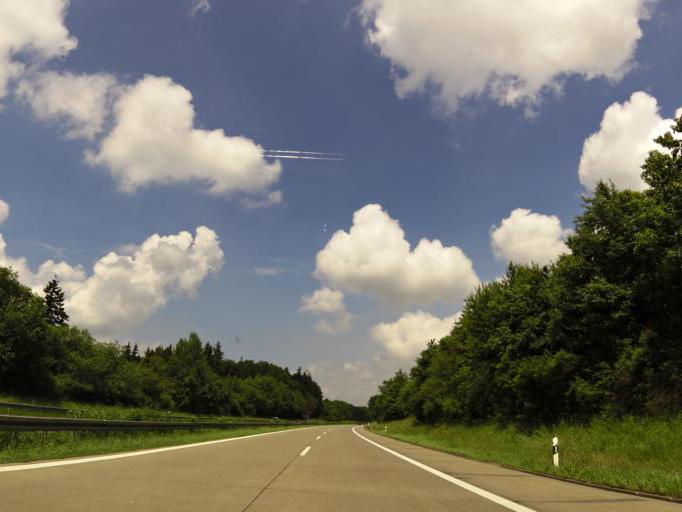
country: DE
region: Baden-Wuerttemberg
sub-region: Regierungsbezirk Stuttgart
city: Westhausen
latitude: 48.8420
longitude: 10.1992
